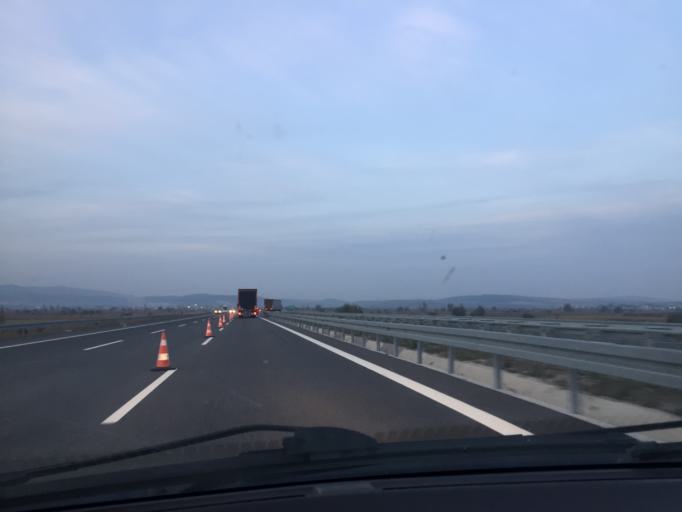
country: TR
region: Manisa
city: Halitpasa
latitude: 38.7420
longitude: 27.6585
